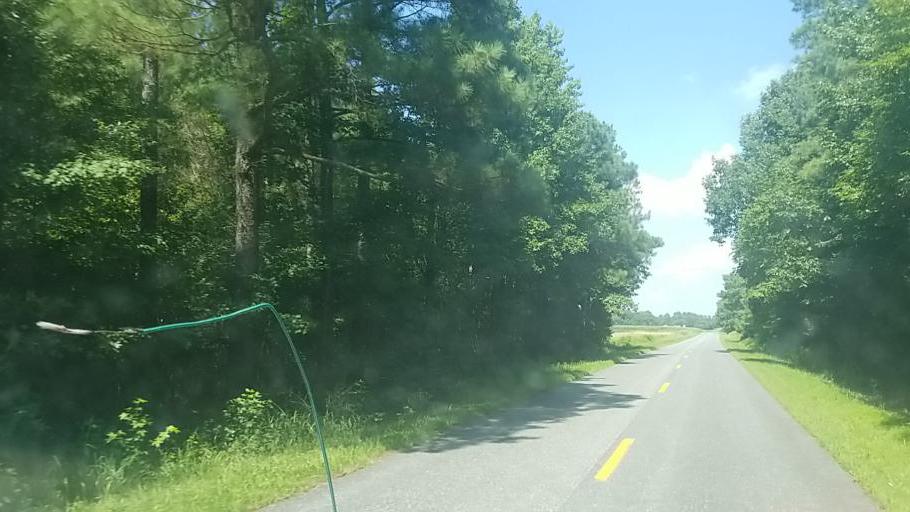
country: US
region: Maryland
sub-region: Wicomico County
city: Hebron
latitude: 38.4314
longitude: -75.8541
